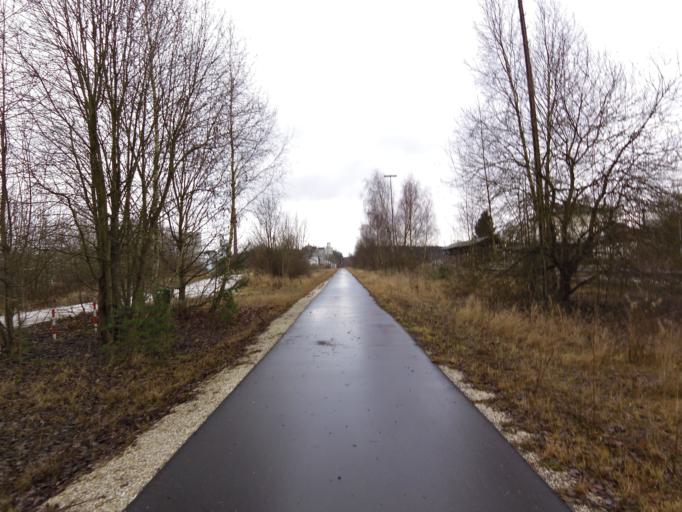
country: DE
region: Bavaria
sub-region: Upper Franconia
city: Wunsiedel
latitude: 50.0522
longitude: 12.0334
